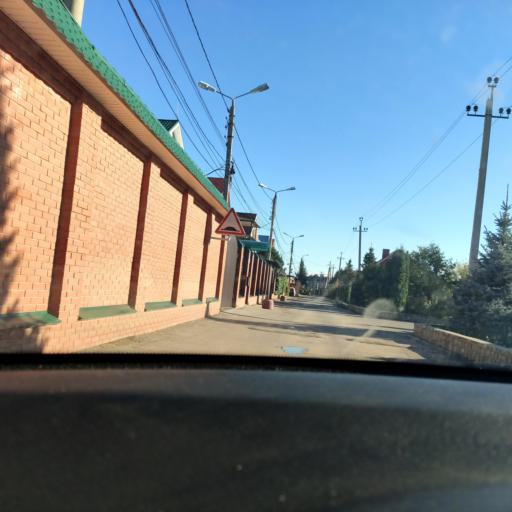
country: RU
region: Samara
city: Samara
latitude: 53.1532
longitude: 50.0824
